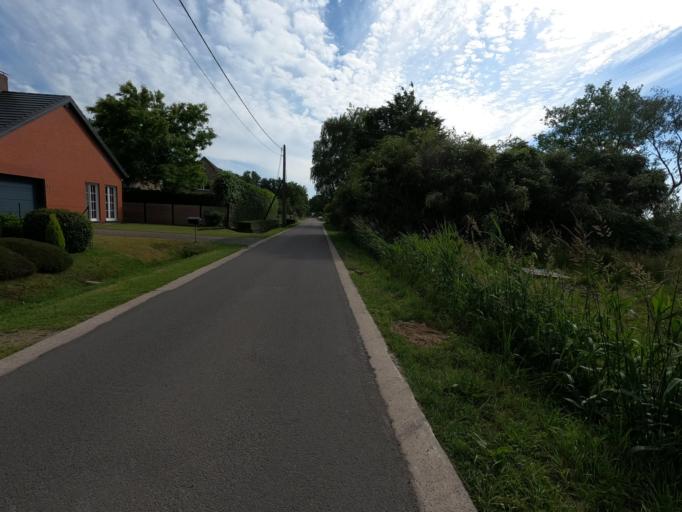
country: BE
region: Flanders
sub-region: Provincie Antwerpen
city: Zandhoven
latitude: 51.2620
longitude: 4.6429
